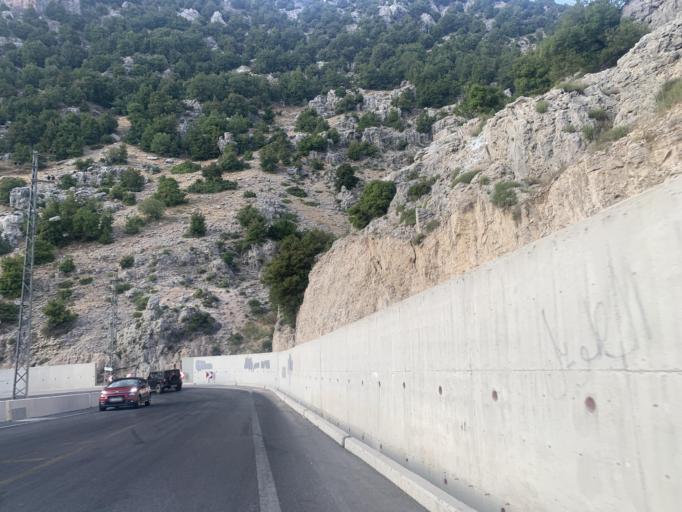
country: LB
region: Liban-Nord
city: Amioun
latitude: 34.1354
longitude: 35.8316
